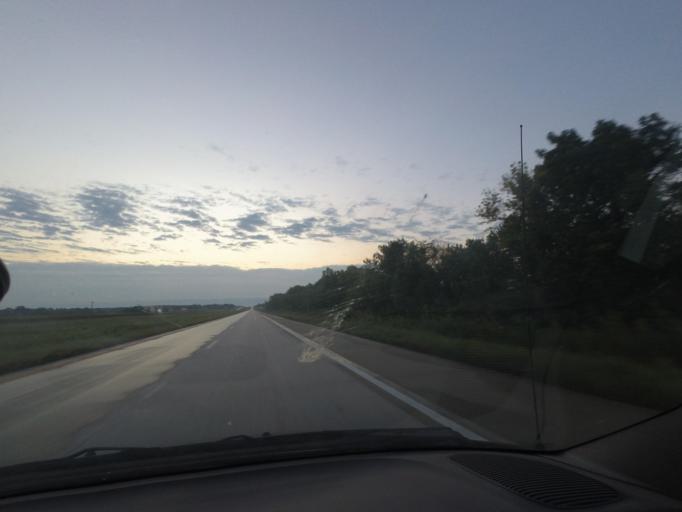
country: US
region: Missouri
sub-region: Macon County
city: Macon
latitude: 39.7599
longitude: -92.6843
